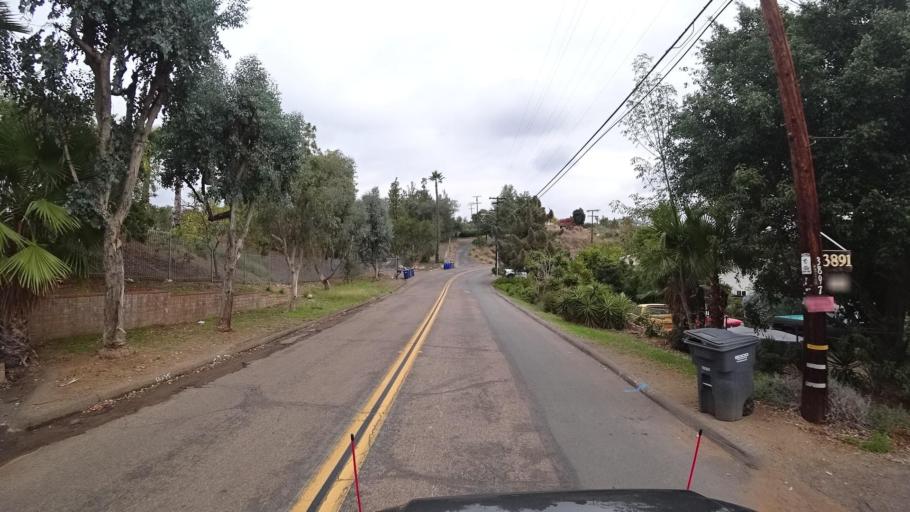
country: US
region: California
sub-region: San Diego County
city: Spring Valley
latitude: 32.7506
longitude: -116.9928
